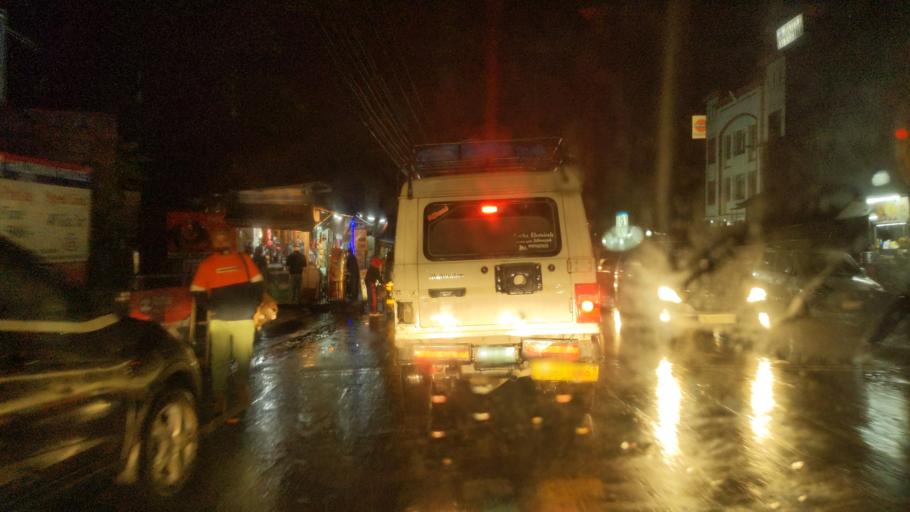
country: IN
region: Uttarakhand
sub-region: Naini Tal
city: Haldwani
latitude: 29.2654
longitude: 79.5446
